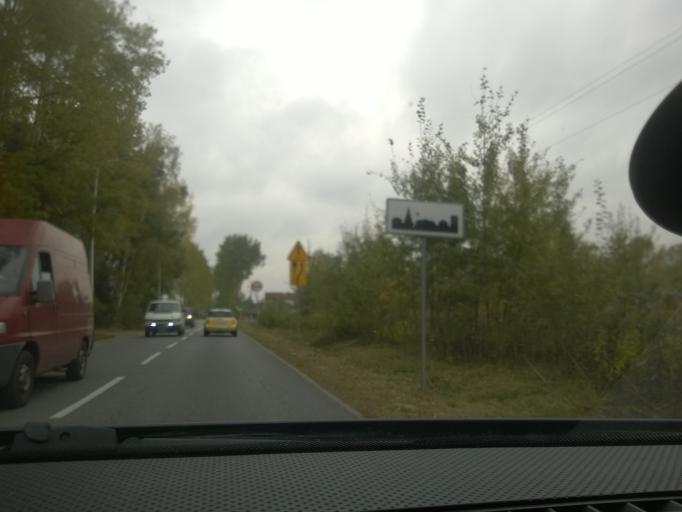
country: PL
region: Masovian Voivodeship
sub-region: Powiat pruszkowski
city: Nadarzyn
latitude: 52.1098
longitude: 20.8004
